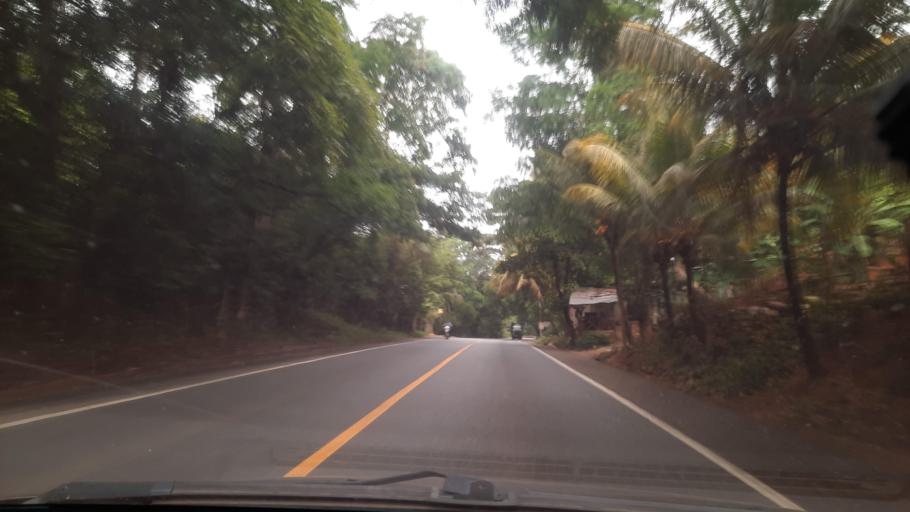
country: GT
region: Izabal
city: Morales
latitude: 15.4388
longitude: -88.9542
